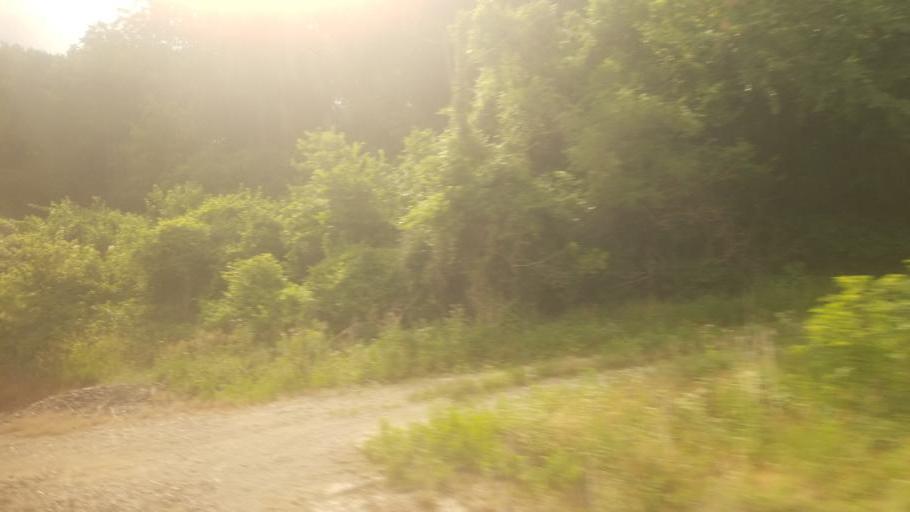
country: US
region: Kansas
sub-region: Douglas County
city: Eudora
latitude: 38.9581
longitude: -95.0752
